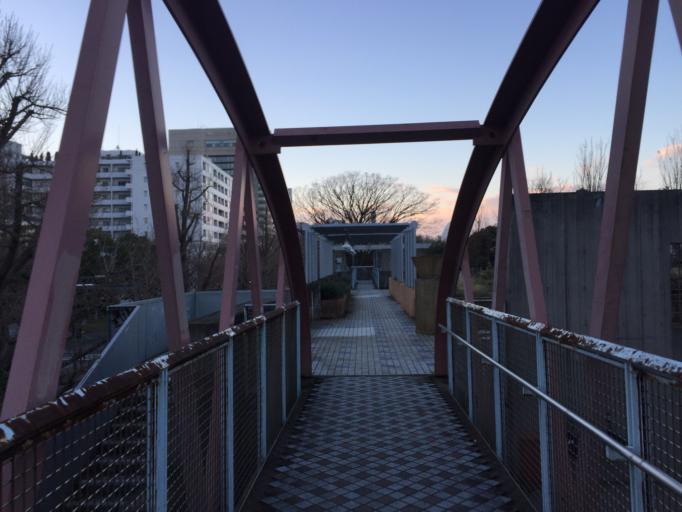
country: JP
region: Kanagawa
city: Yokohama
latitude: 35.4438
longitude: 139.6522
